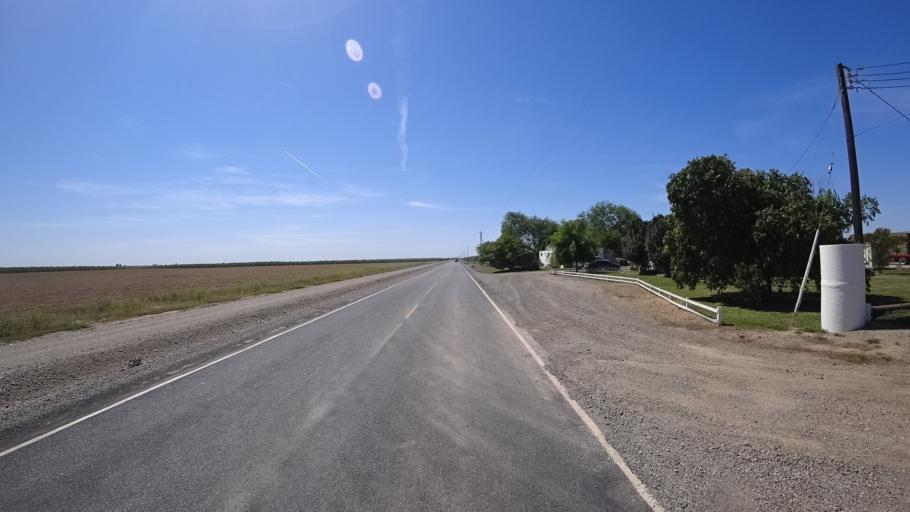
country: US
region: California
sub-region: Glenn County
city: Orland
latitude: 39.6670
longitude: -122.1406
